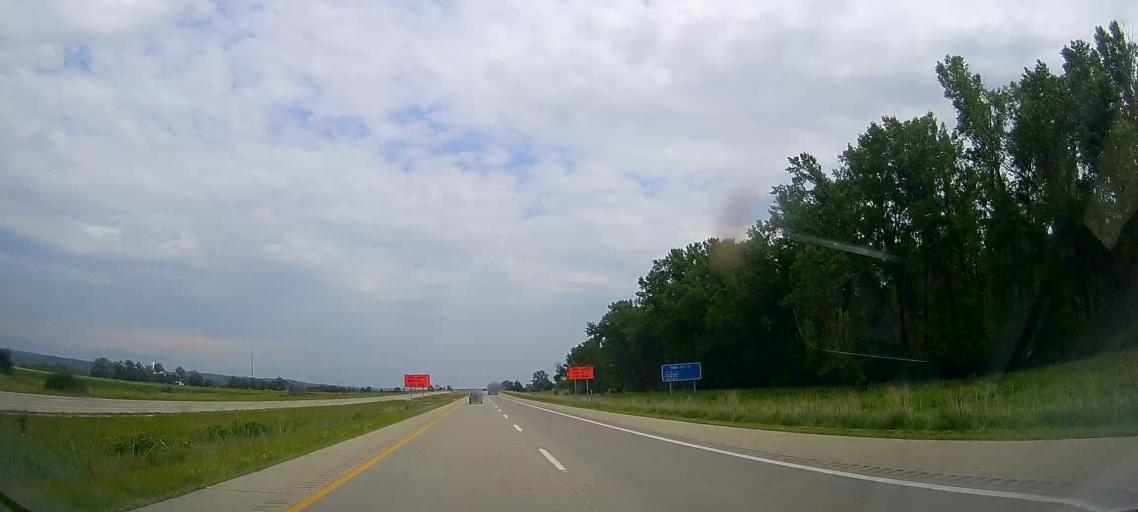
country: US
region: Nebraska
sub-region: Burt County
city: Tekamah
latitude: 41.8097
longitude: -96.0624
